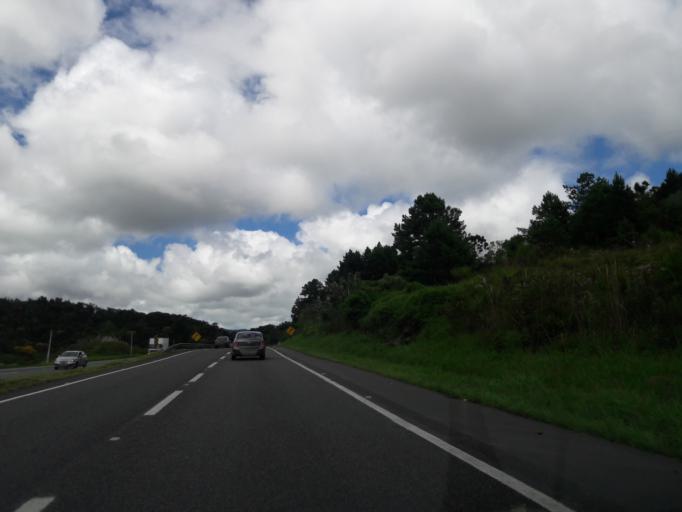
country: BR
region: Parana
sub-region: Antonina
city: Antonina
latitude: -25.0217
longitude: -48.5167
